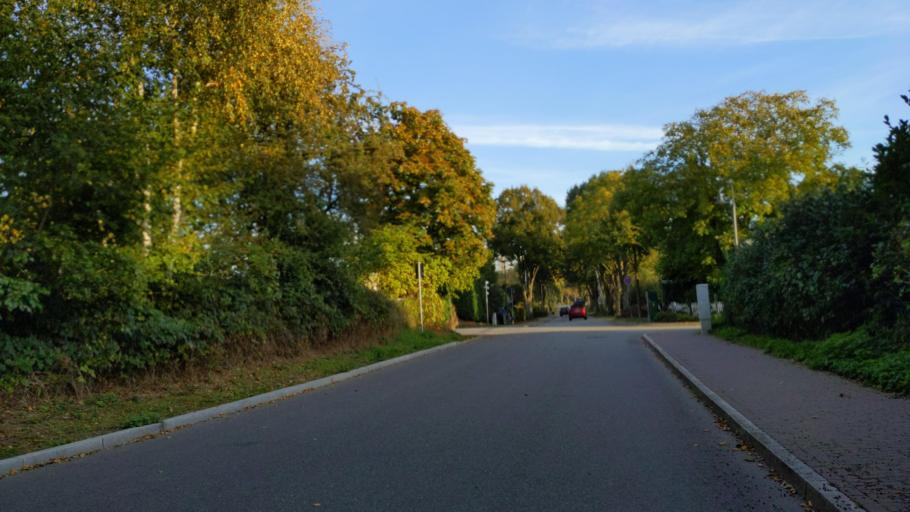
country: DE
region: Schleswig-Holstein
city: Scharbeutz
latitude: 54.0490
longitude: 10.7415
